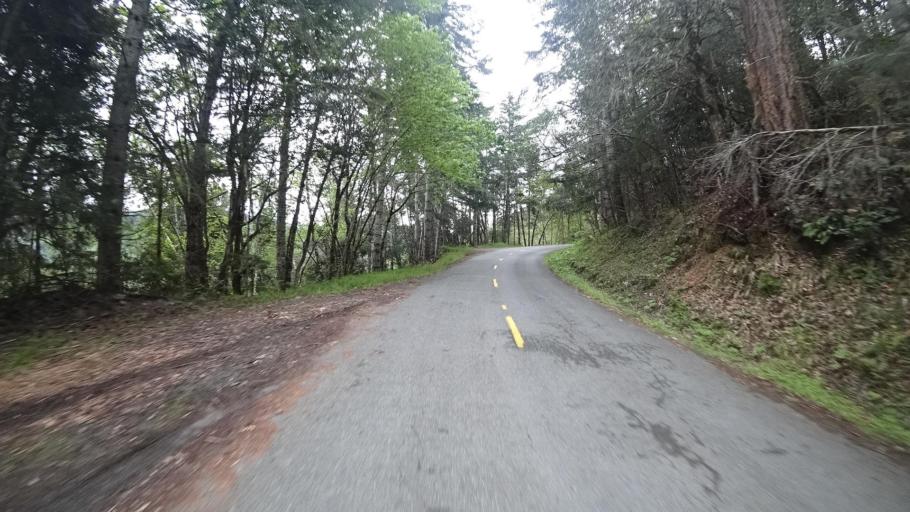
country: US
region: California
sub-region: Humboldt County
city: Blue Lake
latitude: 40.9345
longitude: -123.8497
